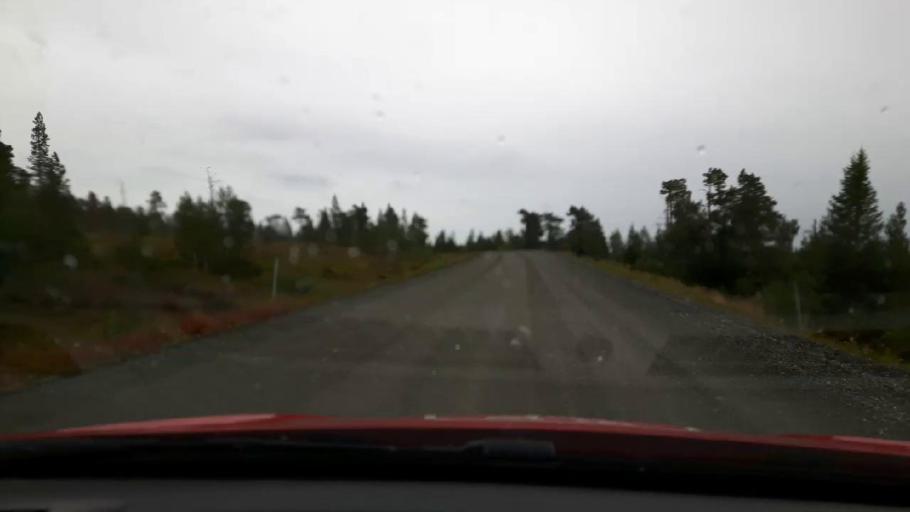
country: NO
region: Nord-Trondelag
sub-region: Meraker
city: Meraker
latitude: 63.6386
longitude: 12.2747
